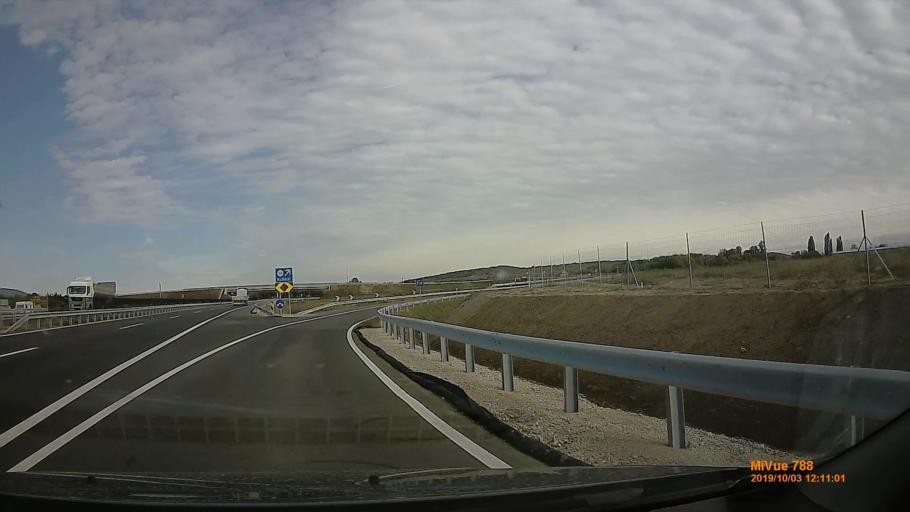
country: HU
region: Pest
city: Szod
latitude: 47.7308
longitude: 19.1611
